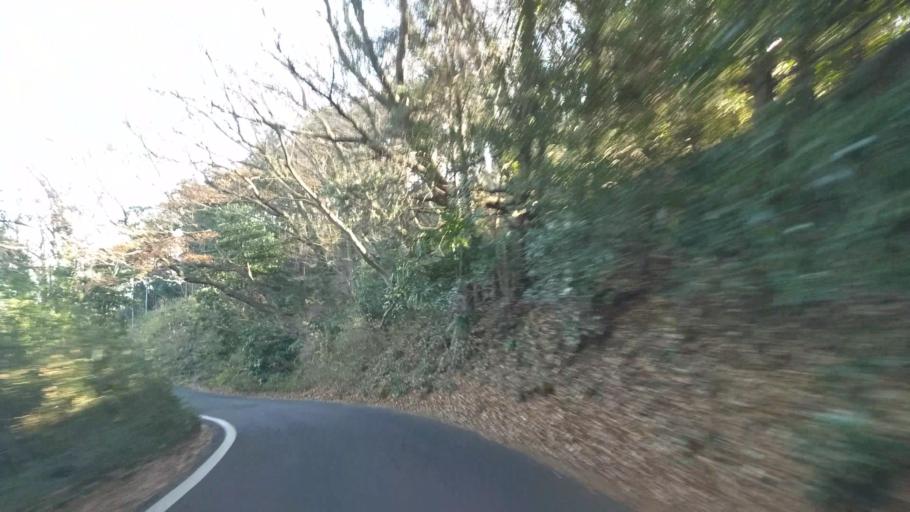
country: JP
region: Kanagawa
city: Hadano
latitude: 35.3690
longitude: 139.2483
